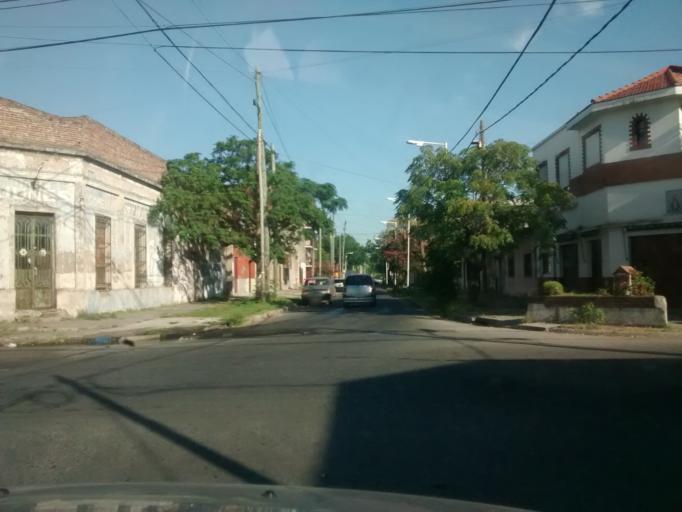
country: AR
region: Buenos Aires
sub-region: Partido de Avellaneda
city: Avellaneda
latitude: -34.6818
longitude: -58.3559
